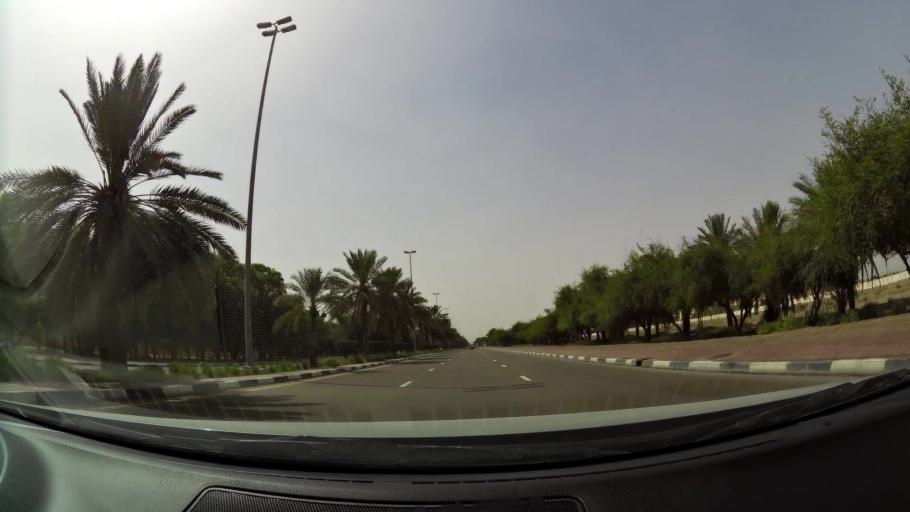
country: AE
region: Abu Dhabi
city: Al Ain
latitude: 24.1795
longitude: 55.6622
